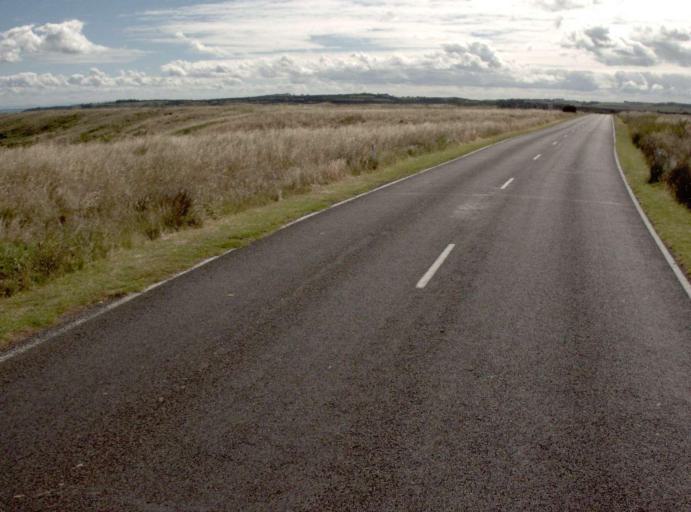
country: AU
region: Victoria
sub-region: Bass Coast
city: Phillip Island
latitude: -38.5110
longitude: 145.1256
